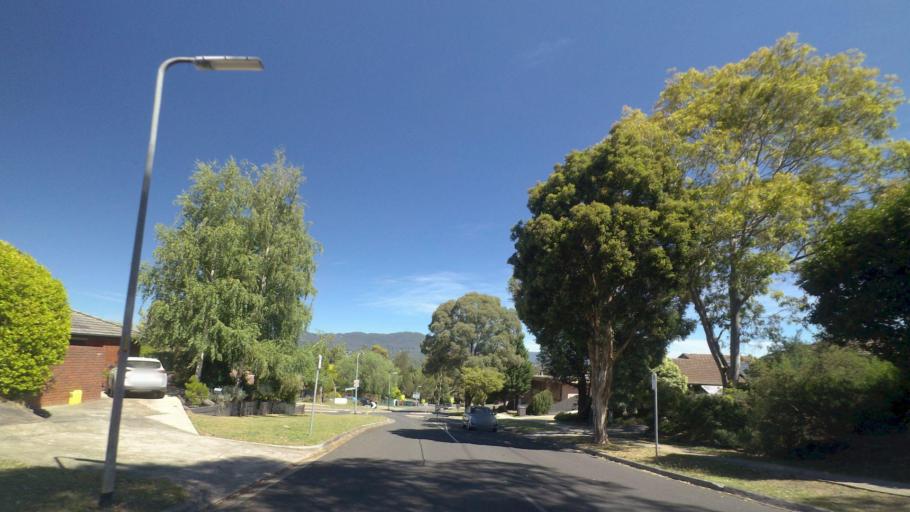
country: AU
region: Victoria
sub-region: Yarra Ranges
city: Lilydale
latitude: -37.7654
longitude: 145.3262
